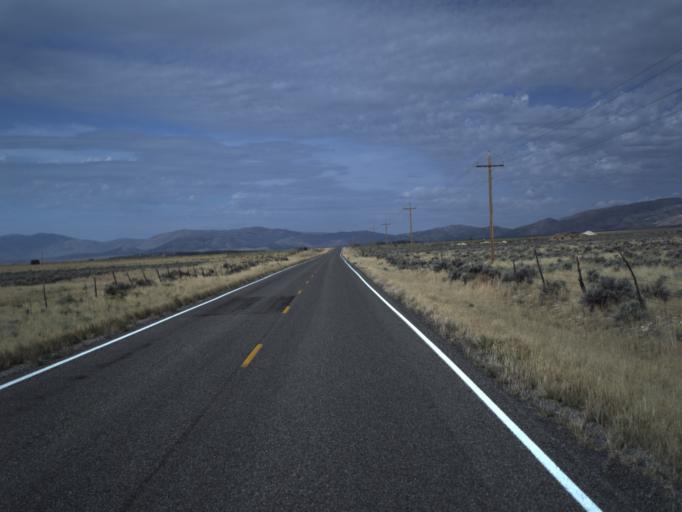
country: US
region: Idaho
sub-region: Cassia County
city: Burley
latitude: 41.8167
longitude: -113.3562
